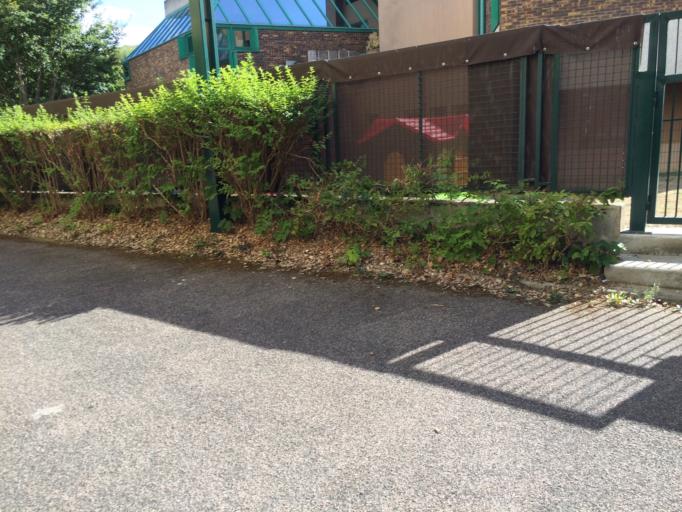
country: FR
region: Ile-de-France
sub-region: Departement de l'Essonne
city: Villebon-sur-Yvette
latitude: 48.7006
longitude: 2.2281
